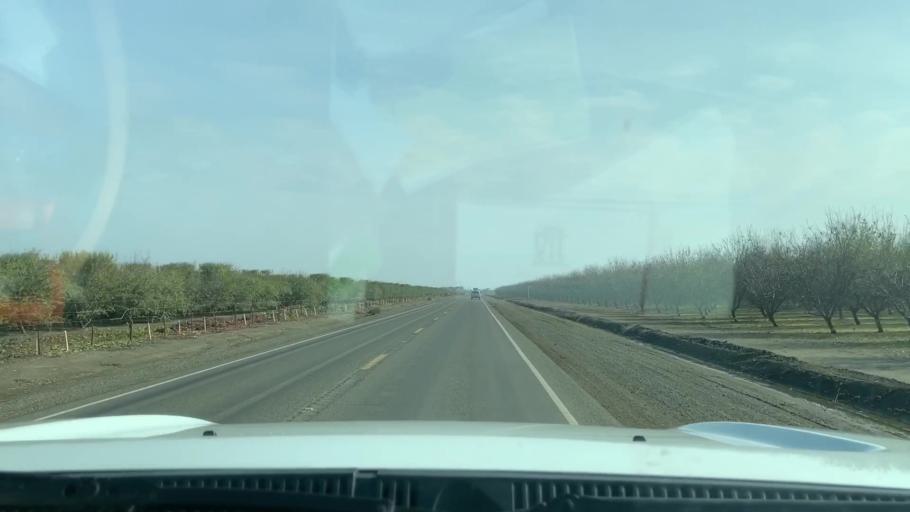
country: US
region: California
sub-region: Fresno County
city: Huron
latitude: 36.2553
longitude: -120.1003
